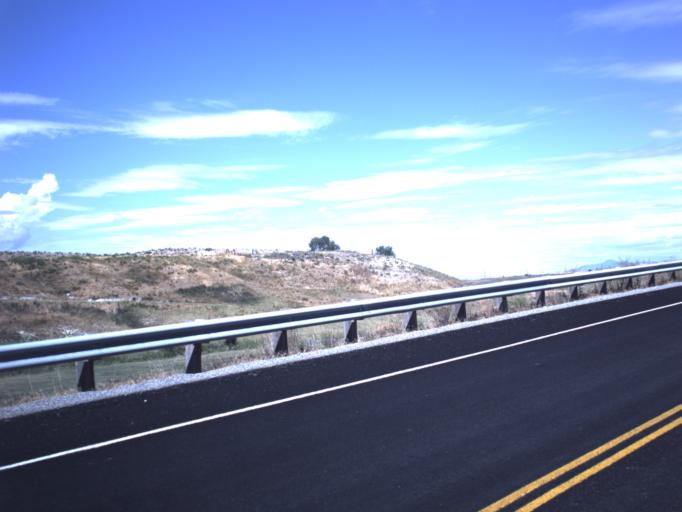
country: US
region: Utah
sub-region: Box Elder County
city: Garland
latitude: 41.8410
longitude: -112.1473
